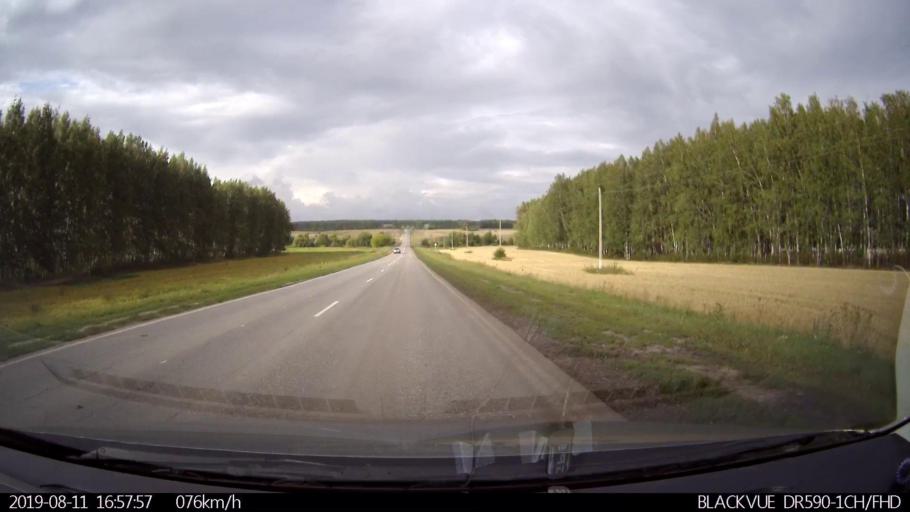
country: RU
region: Ulyanovsk
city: Mayna
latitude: 54.3033
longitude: 47.6548
